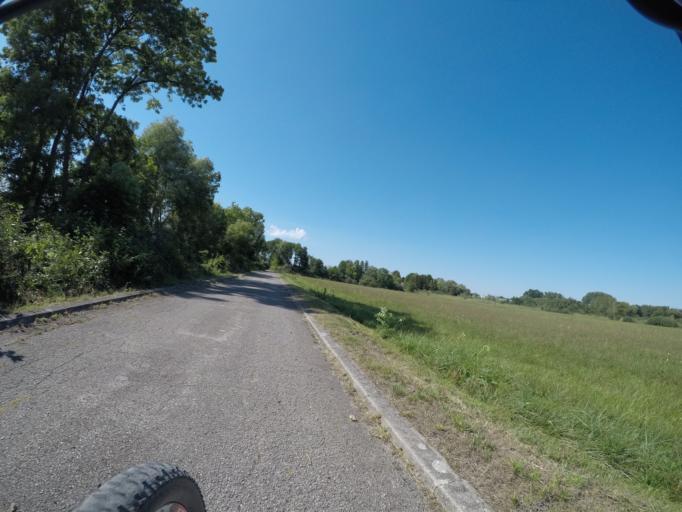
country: AT
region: Lower Austria
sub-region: Politischer Bezirk Wien-Umgebung
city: Moosbrunn
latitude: 48.0086
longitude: 16.4584
